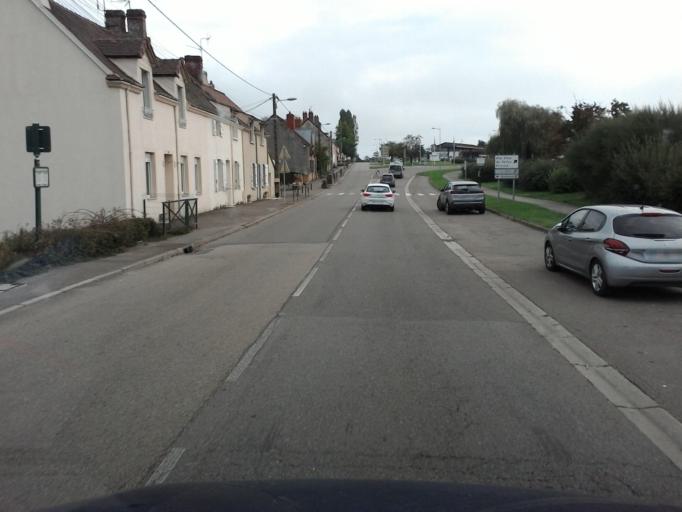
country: FR
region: Bourgogne
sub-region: Departement de Saone-et-Loire
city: Autun
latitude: 46.9559
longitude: 4.3139
